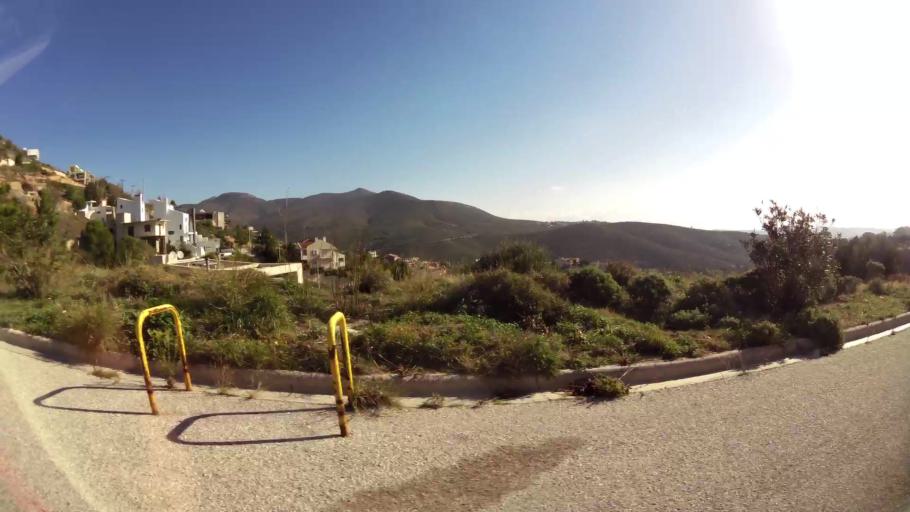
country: GR
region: Attica
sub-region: Nomarchia Anatolikis Attikis
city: Dhrafi
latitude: 38.0362
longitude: 23.8956
